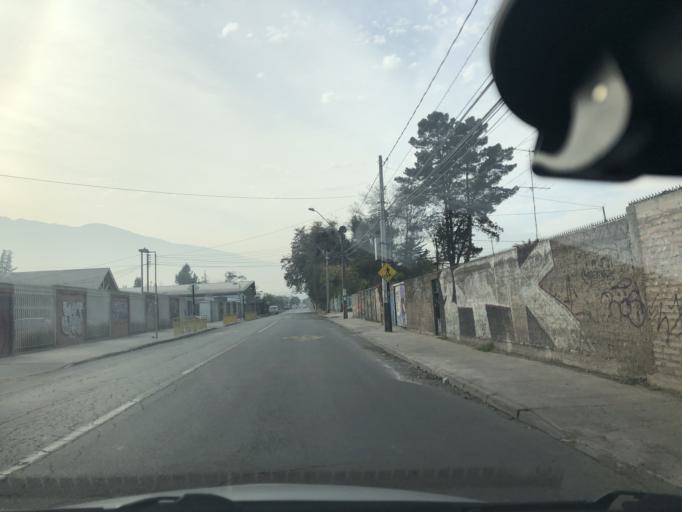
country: CL
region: Santiago Metropolitan
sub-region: Provincia de Cordillera
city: Puente Alto
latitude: -33.5827
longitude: -70.5764
